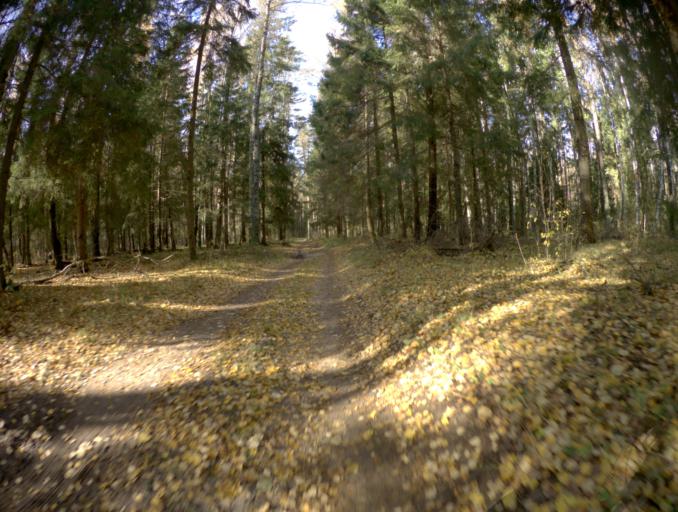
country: RU
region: Vladimir
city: Kommunar
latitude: 56.0490
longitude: 40.4677
